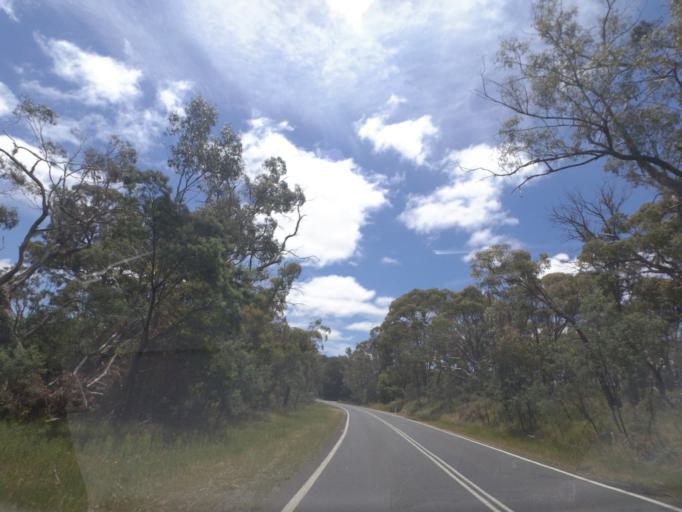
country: AU
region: Victoria
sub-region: Mount Alexander
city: Castlemaine
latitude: -37.3146
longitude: 144.1663
